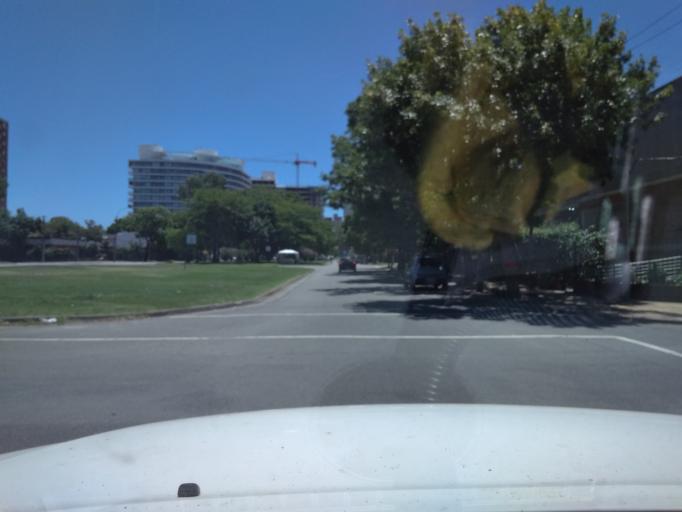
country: UY
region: Canelones
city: Paso de Carrasco
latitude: -34.8899
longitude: -56.1062
